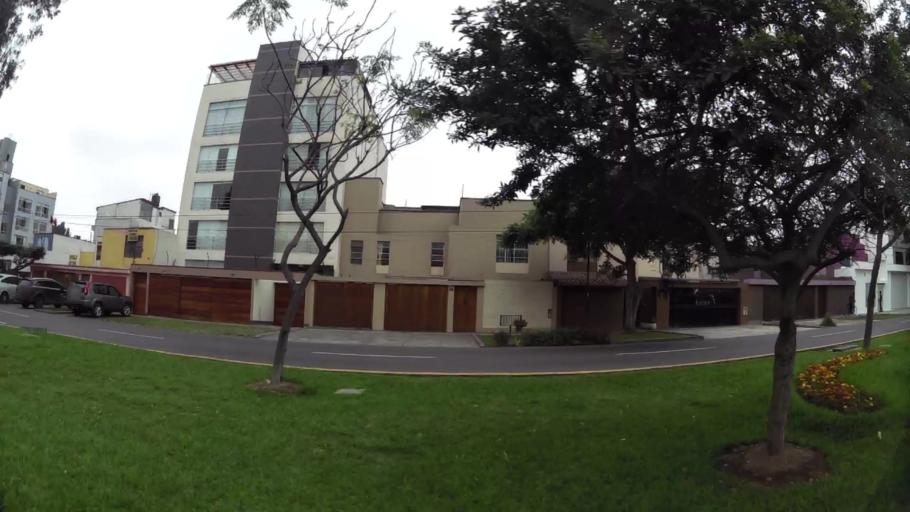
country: PE
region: Lima
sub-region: Lima
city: Surco
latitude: -12.1336
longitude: -76.9897
